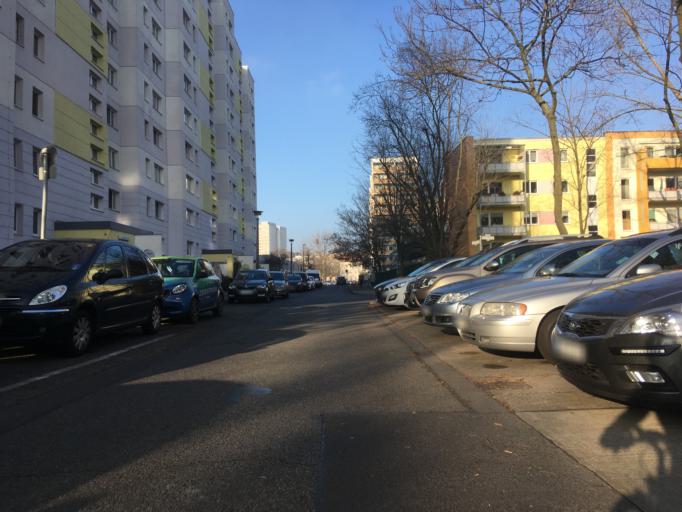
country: DE
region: Berlin
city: Friedrichsfelde
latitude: 52.5031
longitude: 13.5173
